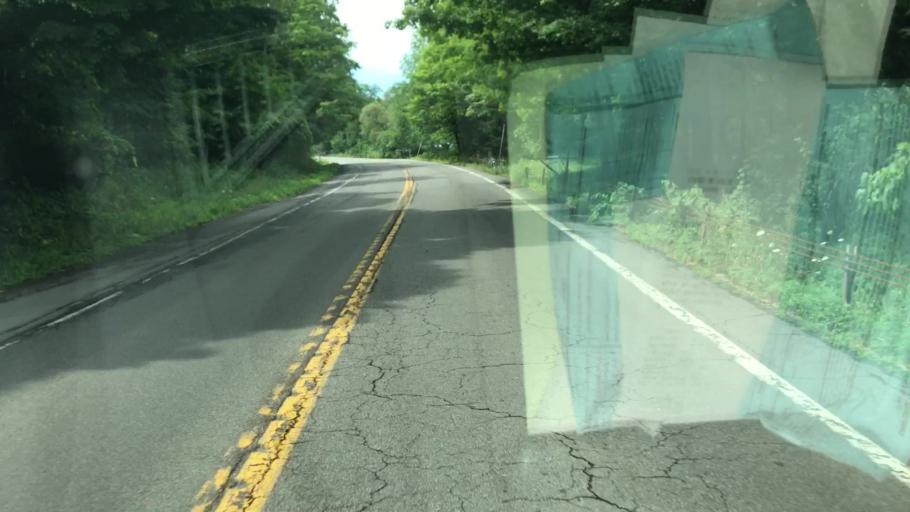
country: US
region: New York
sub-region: Onondaga County
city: Marcellus
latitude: 42.9327
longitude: -76.3407
